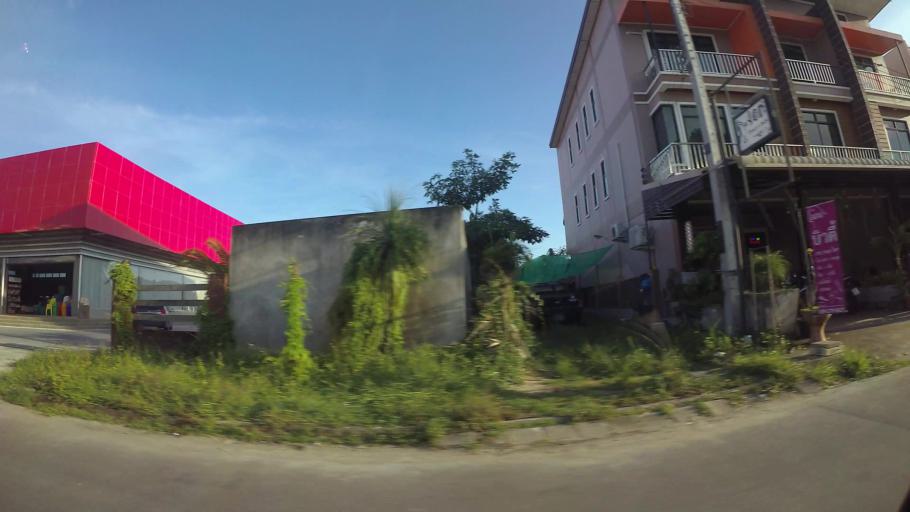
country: TH
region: Rayong
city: Rayong
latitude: 12.6857
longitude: 101.2837
